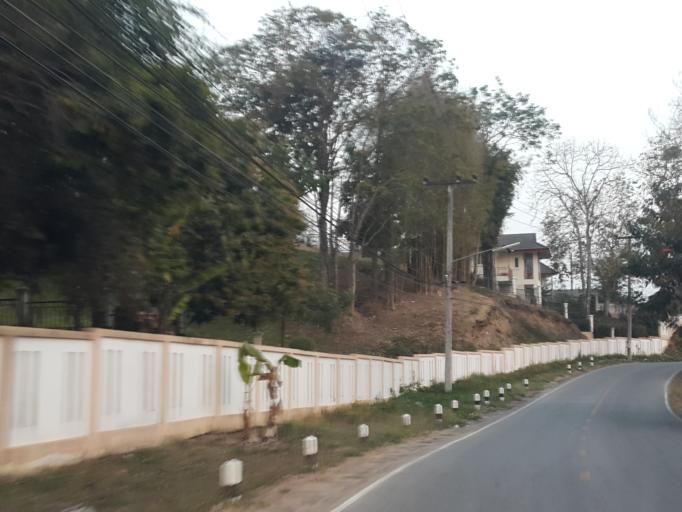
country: TH
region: Chiang Mai
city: Mae Taeng
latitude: 18.9922
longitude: 98.8947
